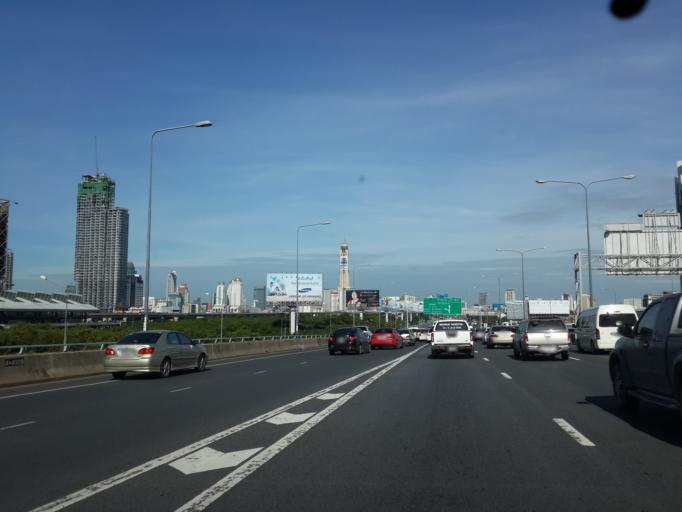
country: TH
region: Bangkok
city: Din Daeng
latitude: 13.7532
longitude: 100.5636
